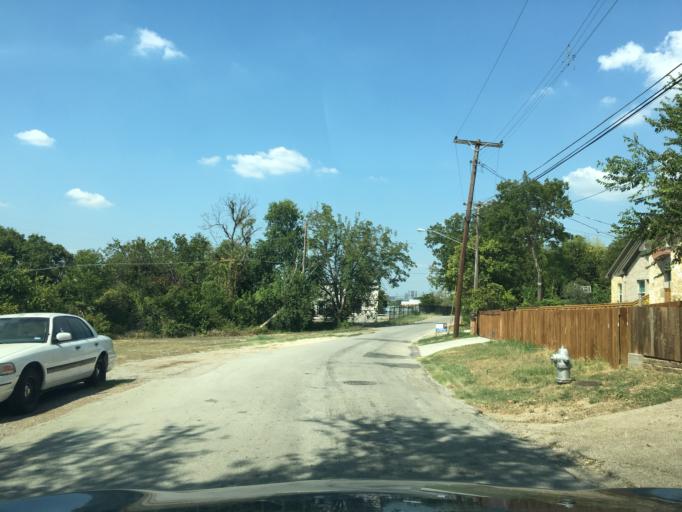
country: US
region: Texas
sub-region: Dallas County
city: Dallas
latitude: 32.7384
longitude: -96.7958
